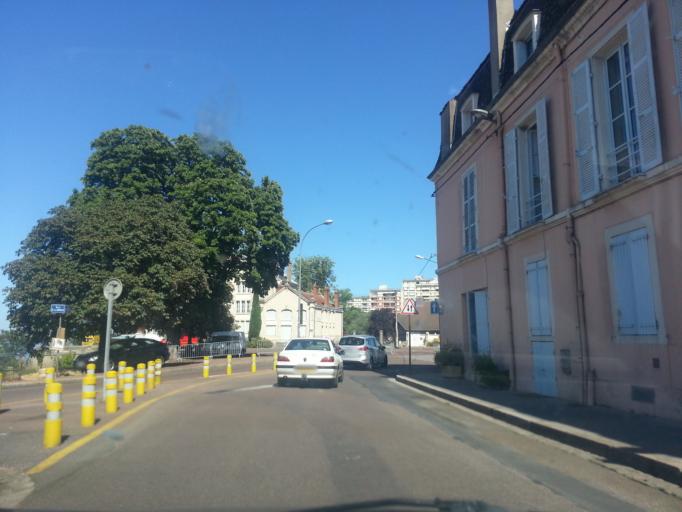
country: FR
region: Bourgogne
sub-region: Departement de Saone-et-Loire
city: Chalon-sur-Saone
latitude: 46.7802
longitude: 4.8613
